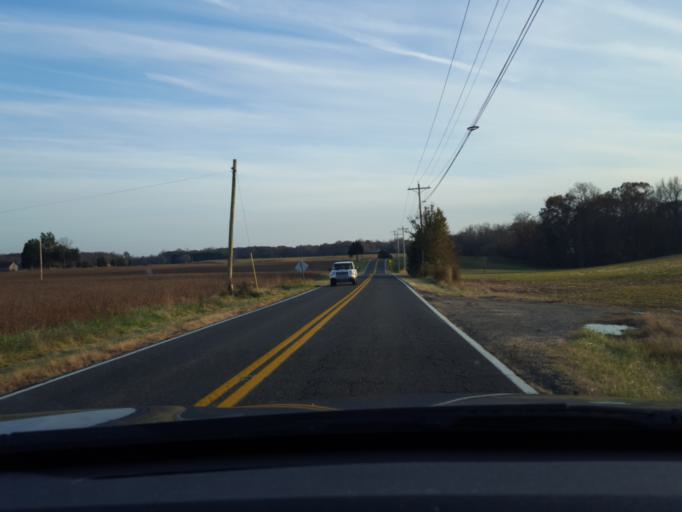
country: US
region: Maryland
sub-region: Saint Mary's County
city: Charlotte Hall
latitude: 38.4908
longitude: -76.8737
